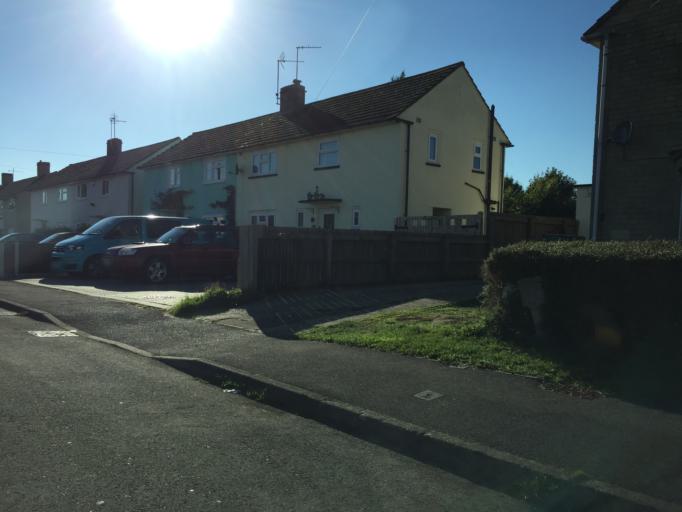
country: GB
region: England
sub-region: Gloucestershire
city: Stonehouse
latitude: 51.7503
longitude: -2.2904
